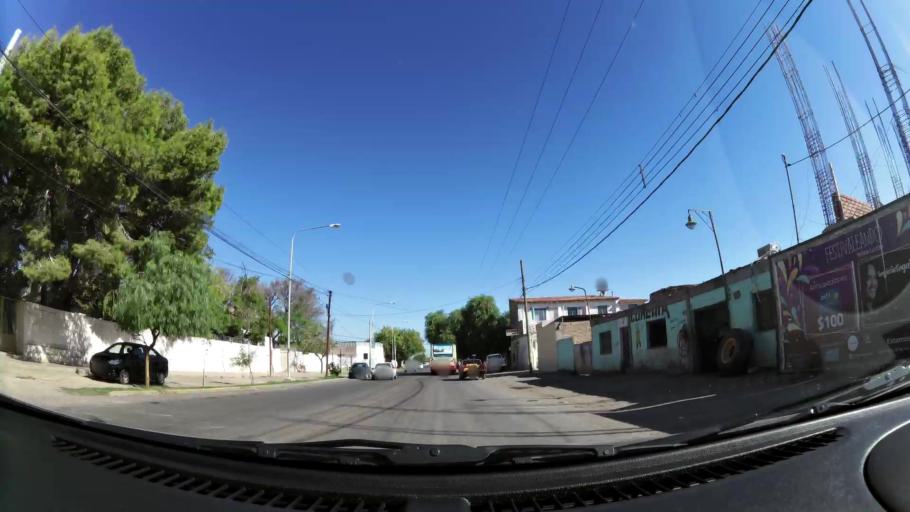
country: AR
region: San Juan
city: Villa Paula de Sarmiento
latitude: -31.5141
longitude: -68.5245
